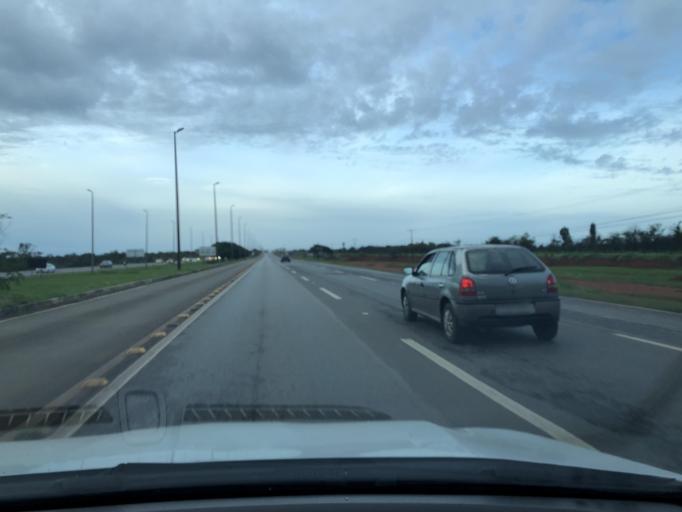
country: BR
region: Federal District
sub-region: Brasilia
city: Brasilia
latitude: -15.9561
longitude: -47.9941
